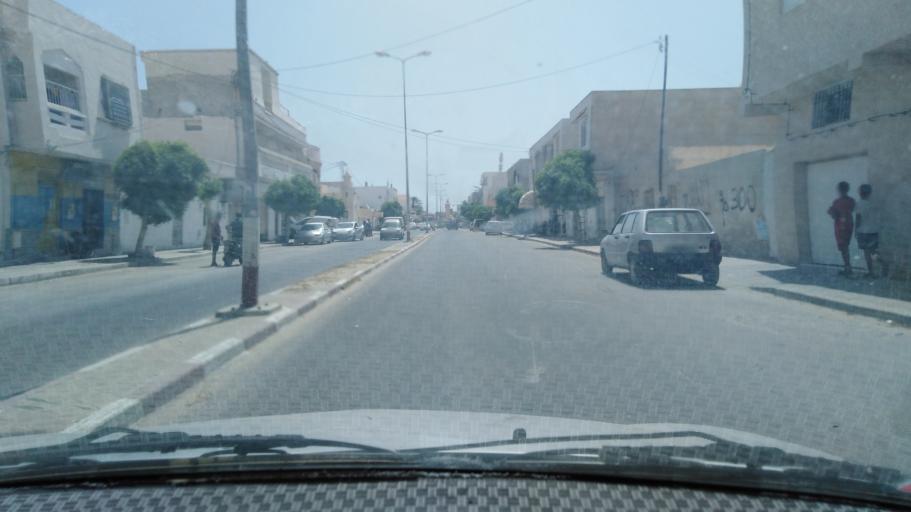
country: TN
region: Qabis
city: Gabes
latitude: 33.9601
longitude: 9.9984
